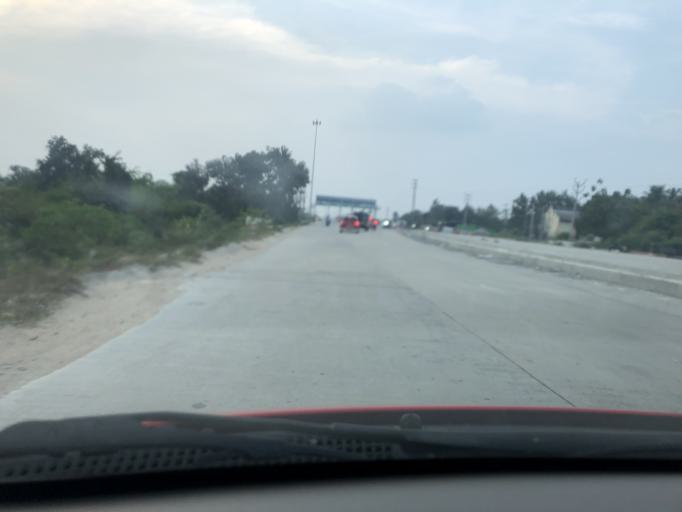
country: IN
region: Andhra Pradesh
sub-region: Chittoor
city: Chittoor
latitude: 13.1947
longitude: 79.0184
